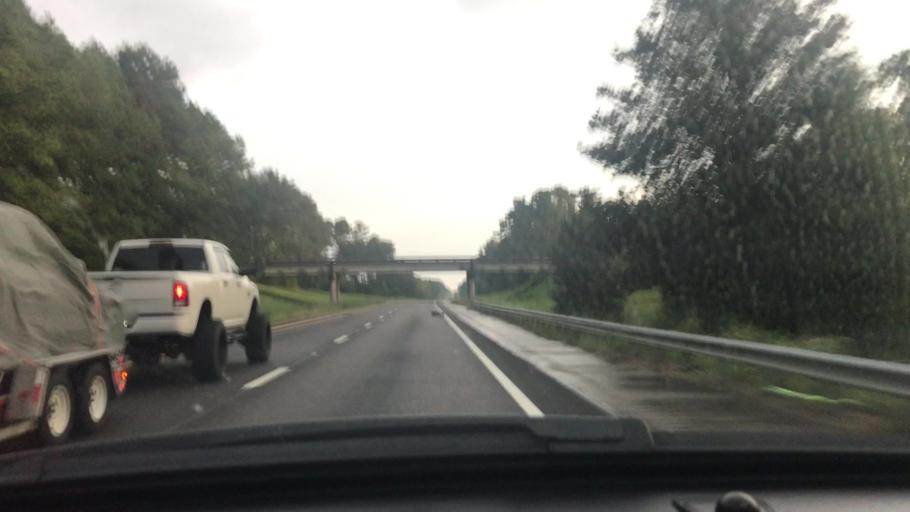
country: US
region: Mississippi
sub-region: Pike County
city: Magnolia
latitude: 31.0650
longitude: -90.4932
